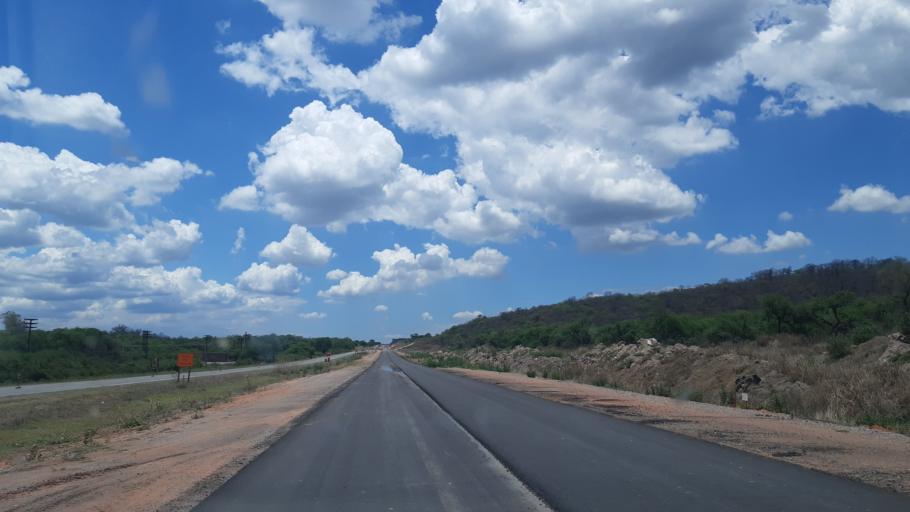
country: AR
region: Jujuy
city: La Mendieta
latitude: -24.4285
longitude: -65.0061
